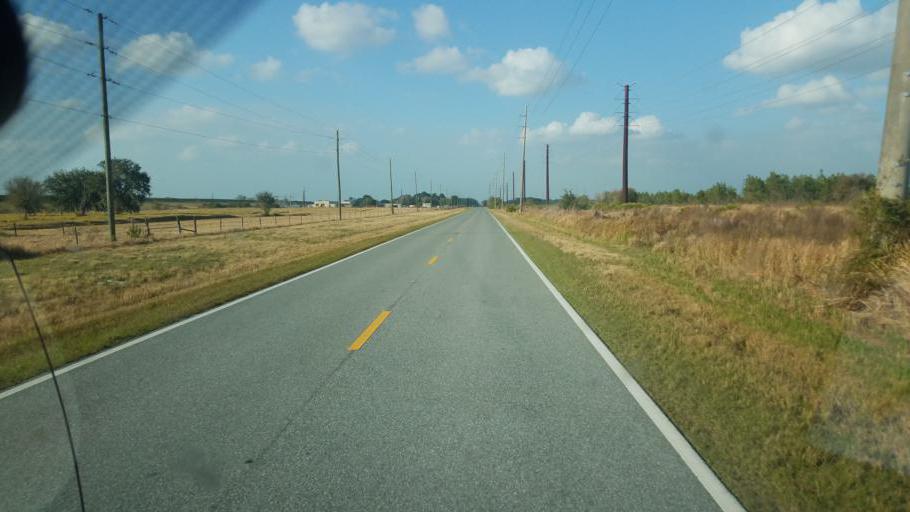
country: US
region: Florida
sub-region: Hardee County
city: Bowling Green
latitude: 27.6235
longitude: -81.9450
